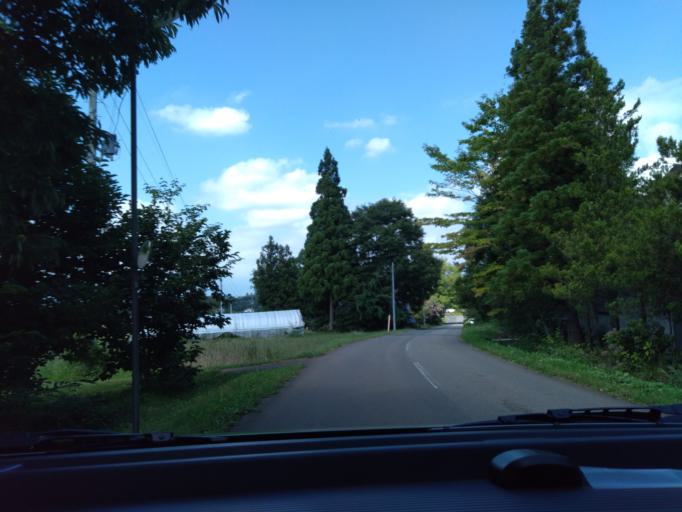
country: JP
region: Iwate
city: Shizukuishi
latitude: 39.6815
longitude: 140.9591
